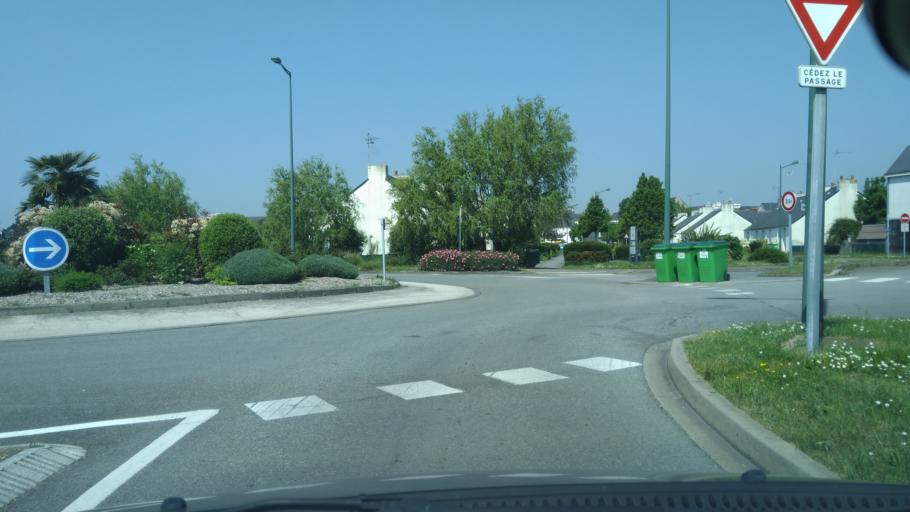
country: FR
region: Pays de la Loire
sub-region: Departement de la Loire-Atlantique
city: Montoir-de-Bretagne
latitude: 47.3257
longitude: -2.1531
